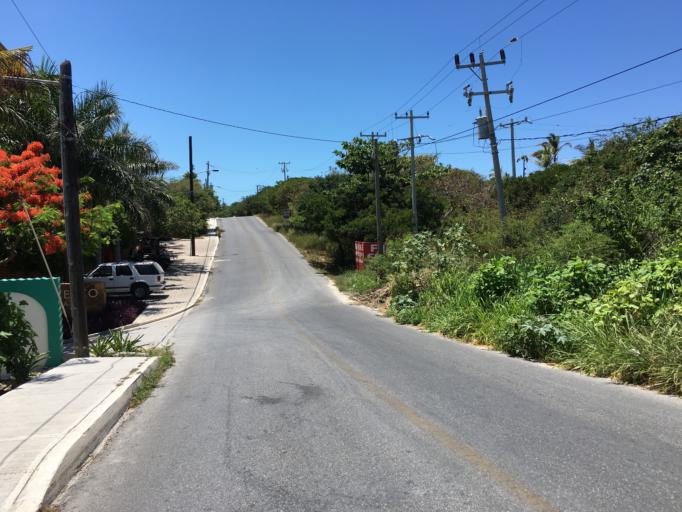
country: MX
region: Quintana Roo
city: Isla Mujeres
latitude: 21.2069
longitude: -86.7180
